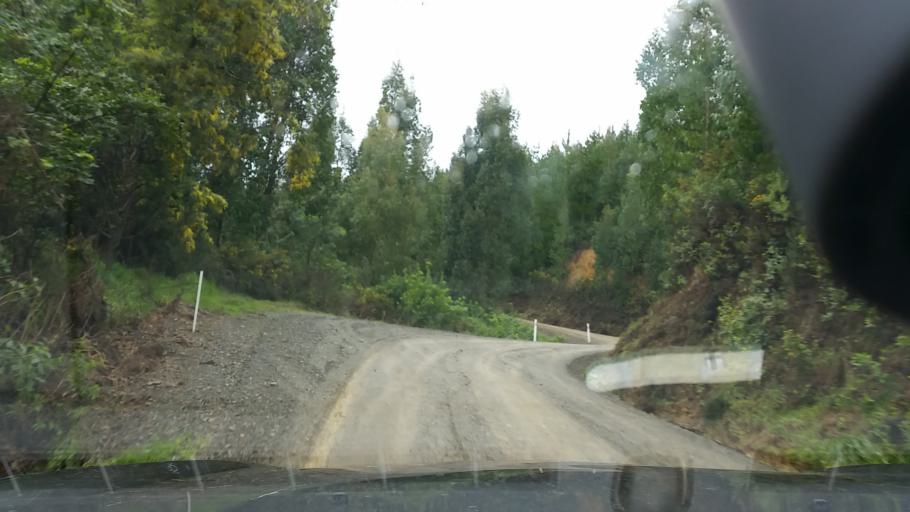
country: NZ
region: Marlborough
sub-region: Marlborough District
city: Picton
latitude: -41.3638
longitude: 174.0716
